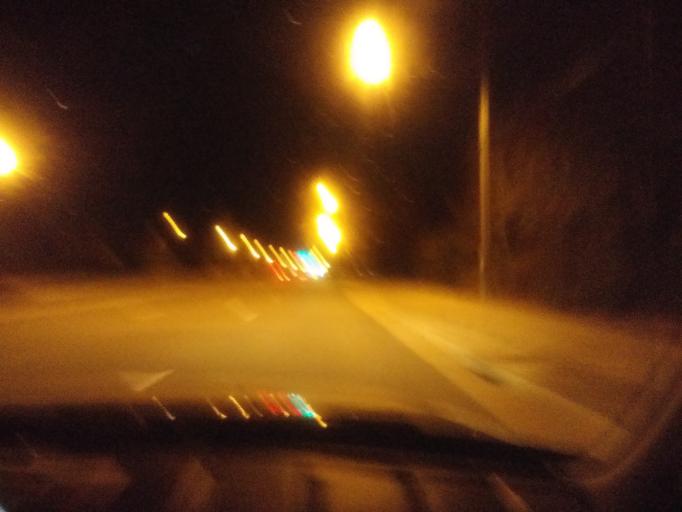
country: US
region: Virginia
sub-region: City of Chesapeake
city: Chesapeake
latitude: 36.7753
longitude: -76.1996
